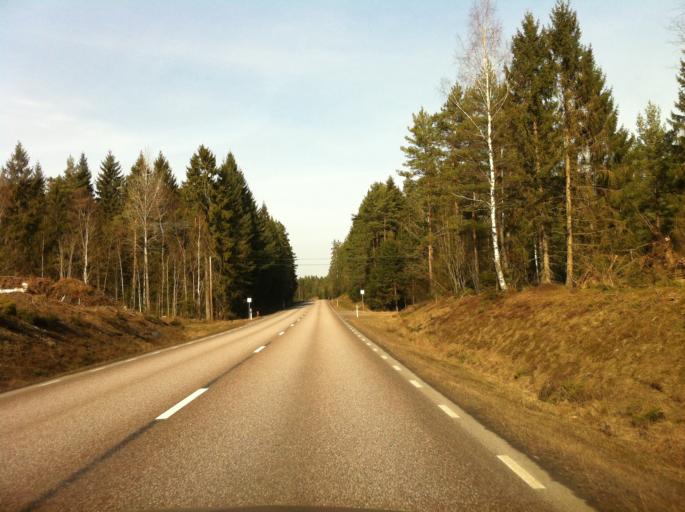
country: SE
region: Vaestra Goetaland
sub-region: Skovde Kommun
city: Skultorp
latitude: 58.2717
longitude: 13.8100
